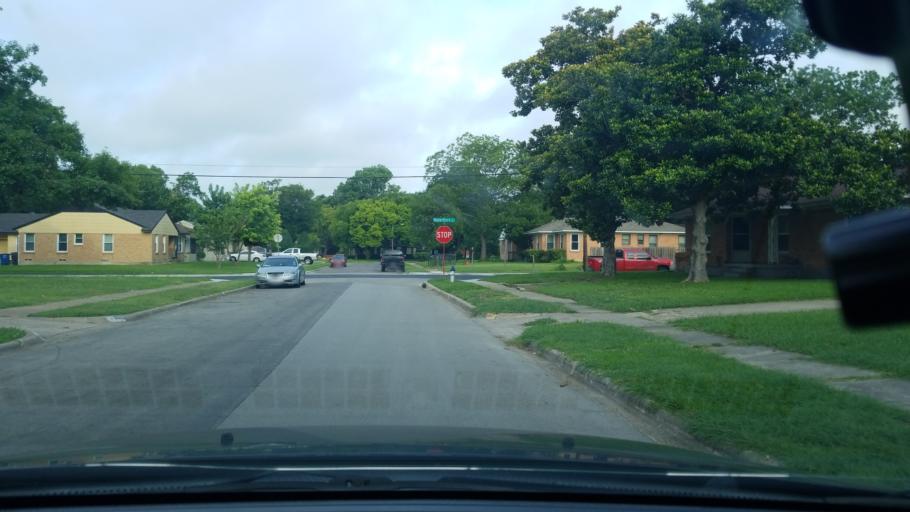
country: US
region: Texas
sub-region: Dallas County
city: Garland
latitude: 32.8304
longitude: -96.6632
